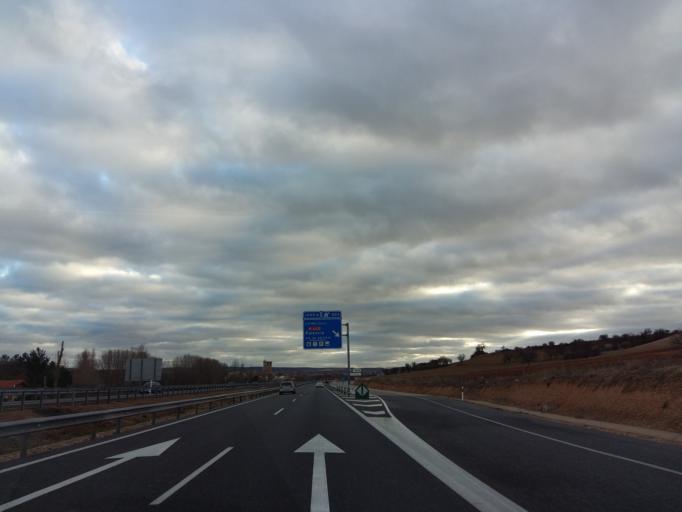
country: ES
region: Castille and Leon
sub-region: Provincia de Burgos
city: Villalmanzo
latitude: 42.0557
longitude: -3.7432
